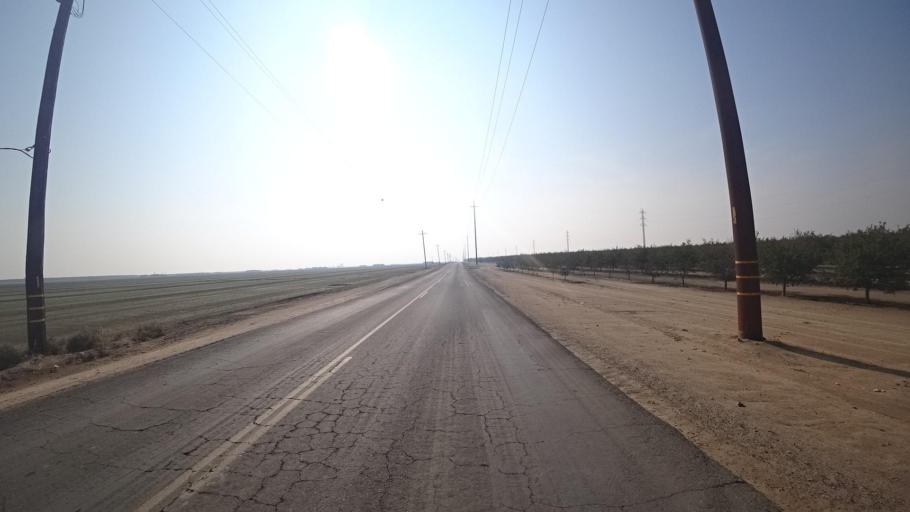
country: US
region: California
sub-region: Kern County
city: Buttonwillow
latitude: 35.4318
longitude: -119.4470
